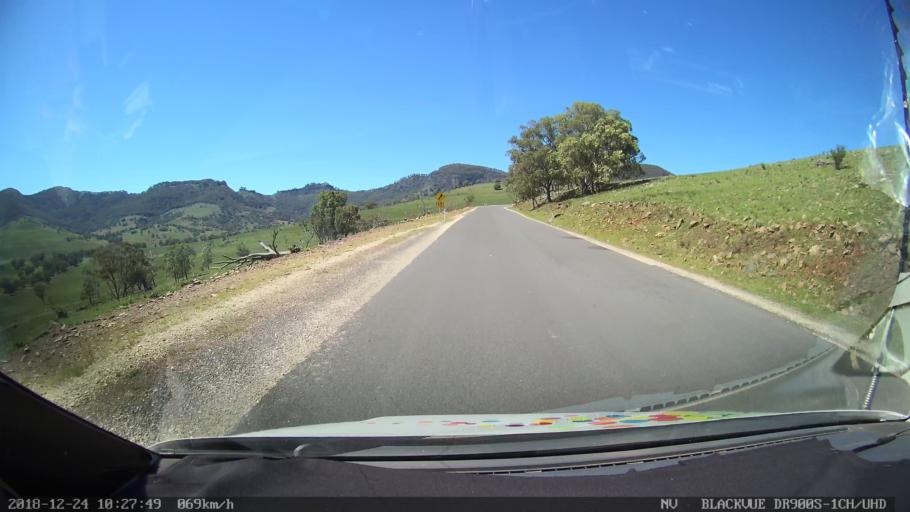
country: AU
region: New South Wales
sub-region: Liverpool Plains
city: Quirindi
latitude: -31.8213
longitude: 150.5337
